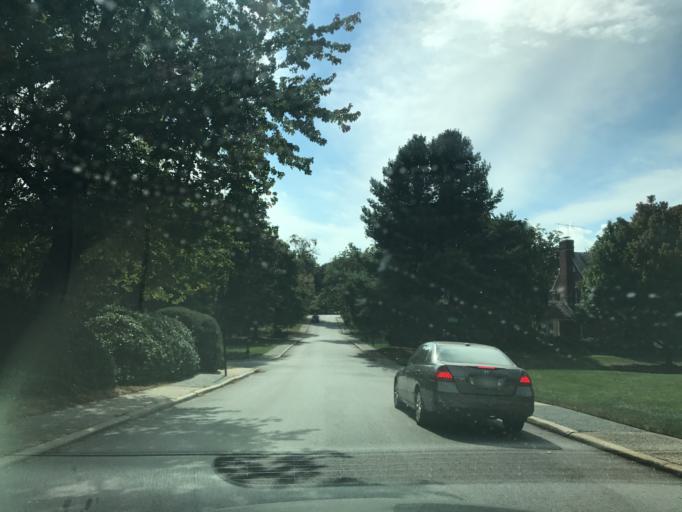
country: US
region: Maryland
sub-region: Baltimore County
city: Towson
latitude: 39.3566
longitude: -76.6207
